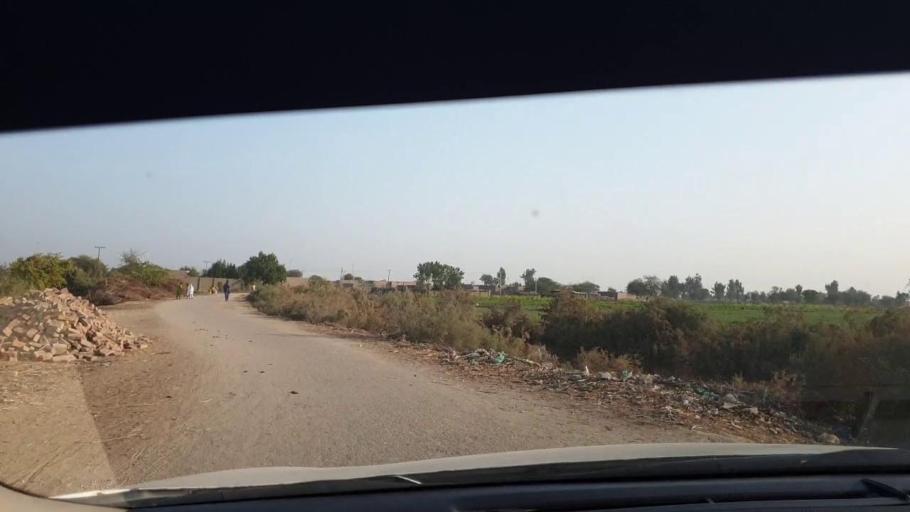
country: PK
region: Sindh
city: Berani
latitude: 25.8431
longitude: 68.7765
